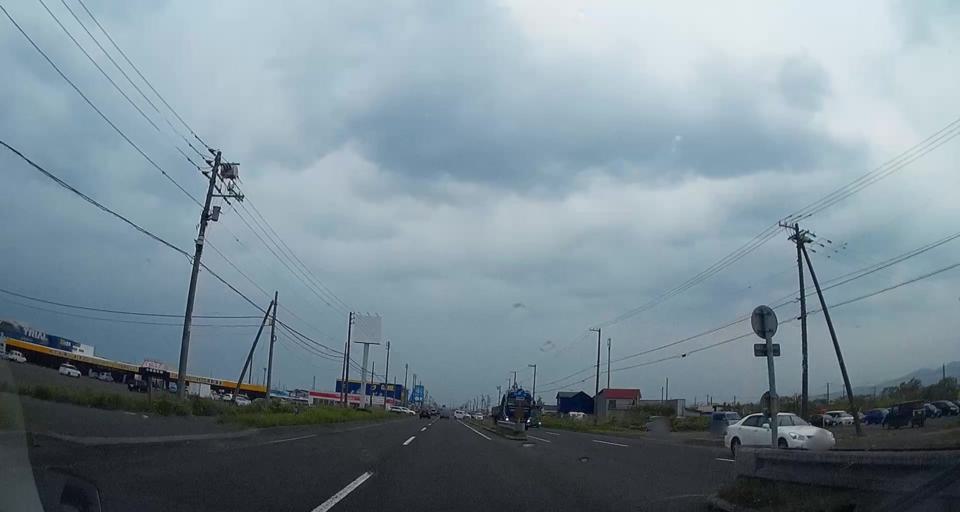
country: JP
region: Hokkaido
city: Tomakomai
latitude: 42.6144
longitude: 141.5254
